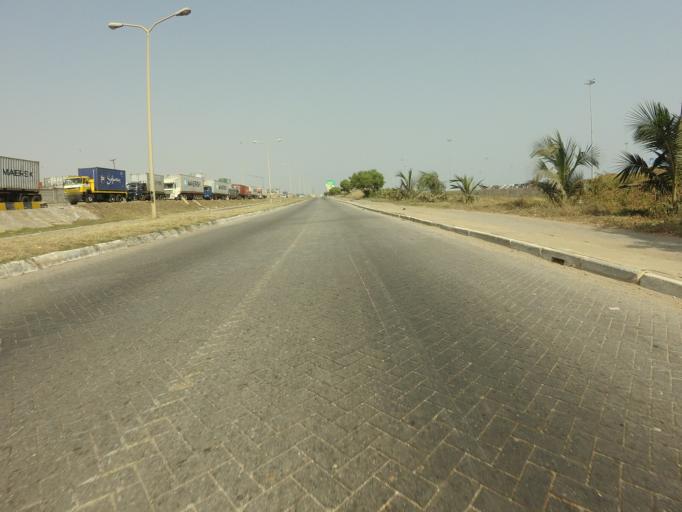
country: GH
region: Greater Accra
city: Tema
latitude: 5.6179
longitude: -0.0187
